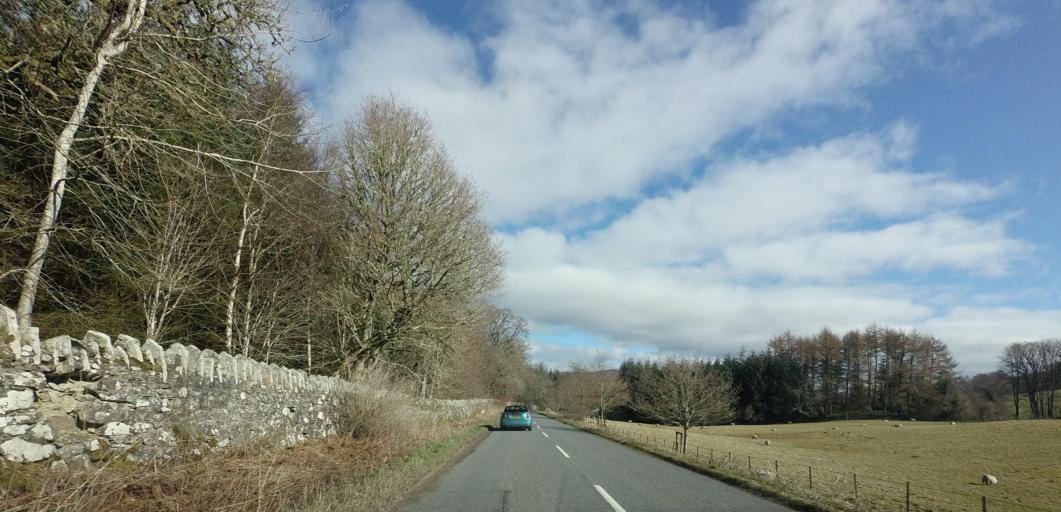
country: GB
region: Scotland
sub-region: Perth and Kinross
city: Aberfeldy
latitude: 56.5986
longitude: -3.9652
